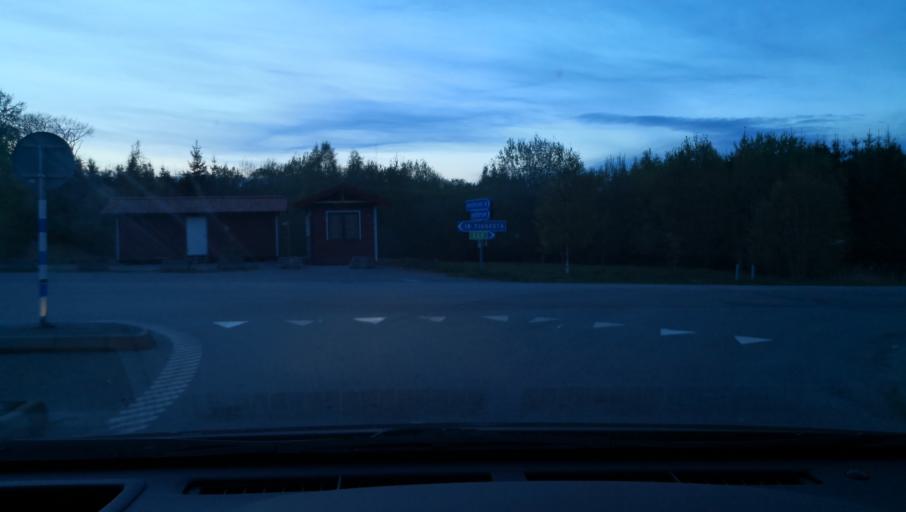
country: SE
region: OErebro
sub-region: Lekebergs Kommun
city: Fjugesta
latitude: 59.0325
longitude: 14.8632
